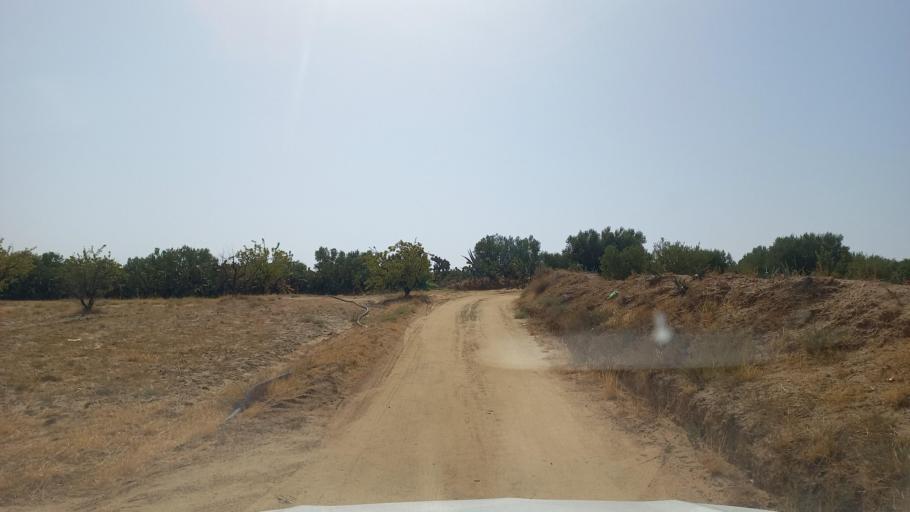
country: TN
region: Al Qasrayn
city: Kasserine
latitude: 35.2367
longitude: 9.0550
